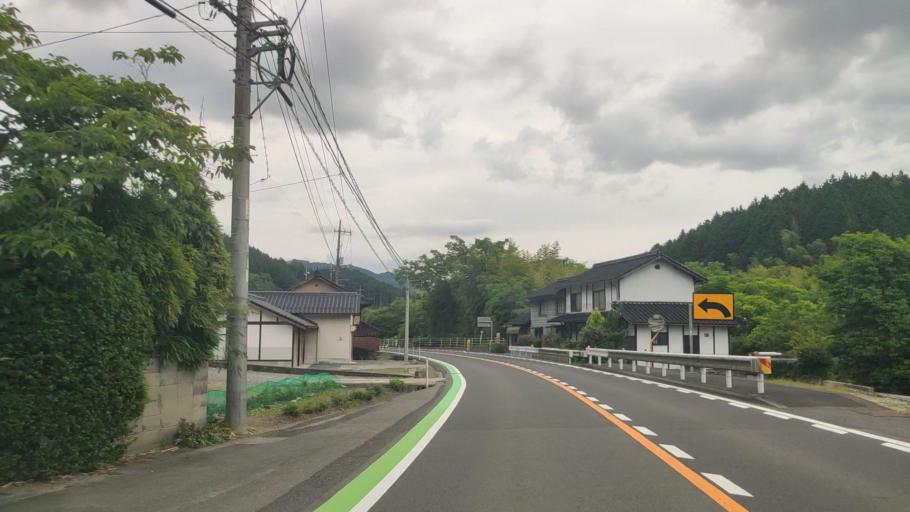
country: JP
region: Okayama
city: Tsuyama
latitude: 35.0623
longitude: 133.8373
